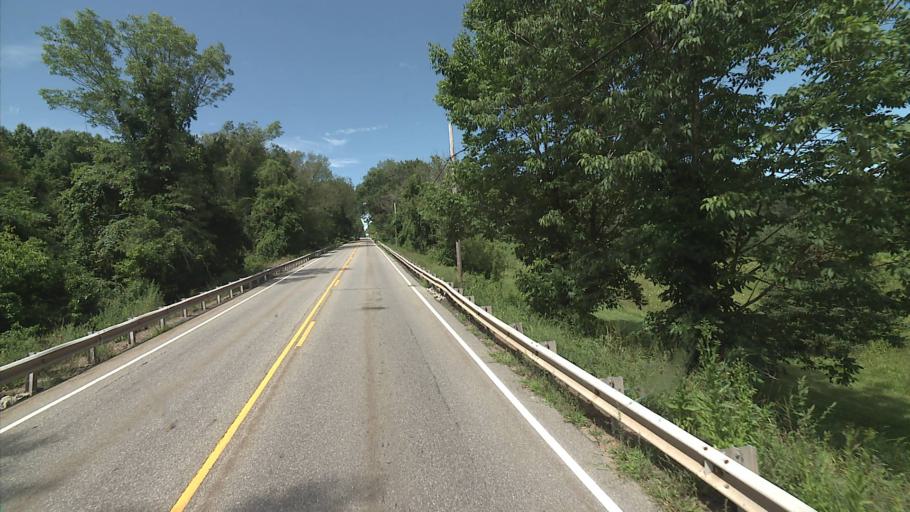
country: US
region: Connecticut
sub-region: Tolland County
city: Mansfield City
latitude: 41.7816
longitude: -72.2148
